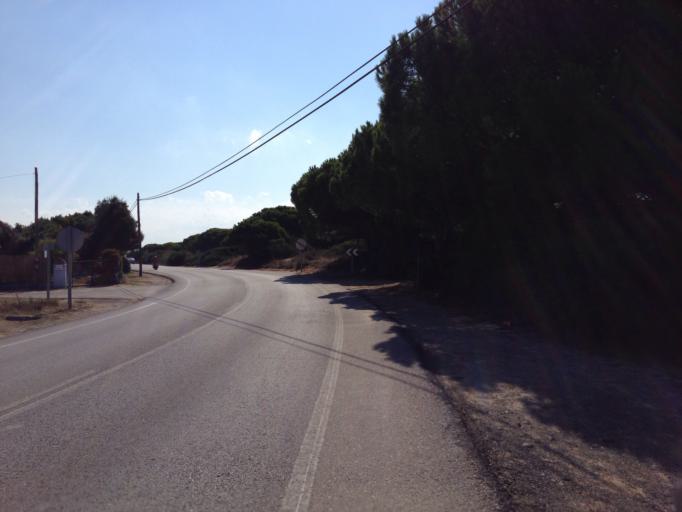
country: ES
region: Andalusia
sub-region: Provincia de Cadiz
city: Vejer de la Frontera
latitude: 36.1885
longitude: -6.0238
